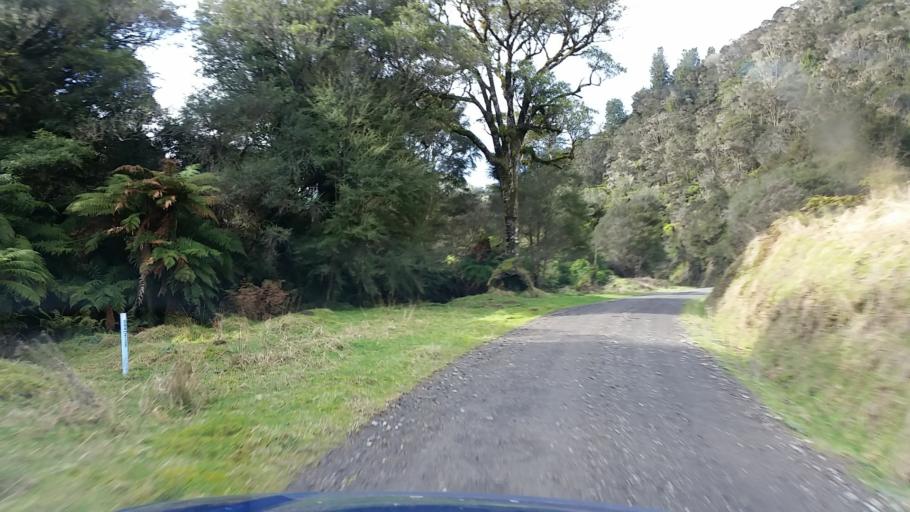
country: NZ
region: Taranaki
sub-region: South Taranaki District
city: Eltham
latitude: -39.2604
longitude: 174.7868
